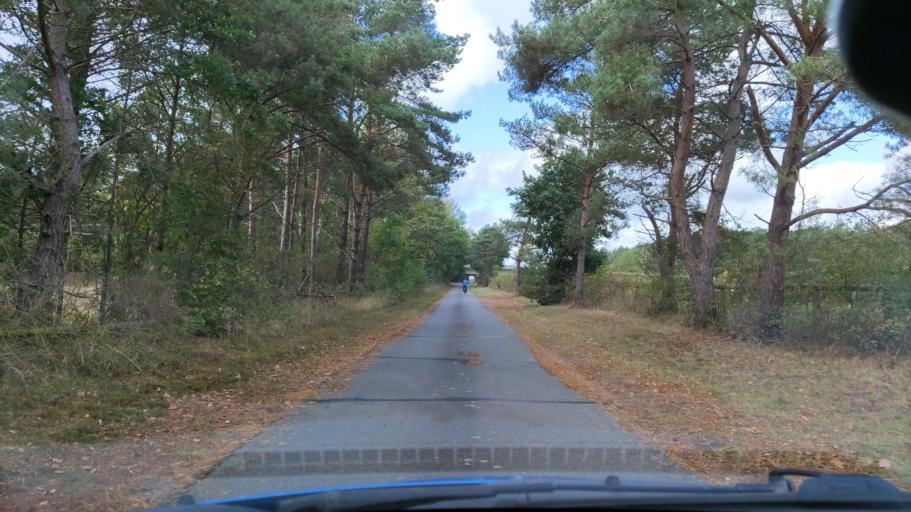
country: DE
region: Lower Saxony
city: Vastorf
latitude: 53.1702
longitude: 10.5209
